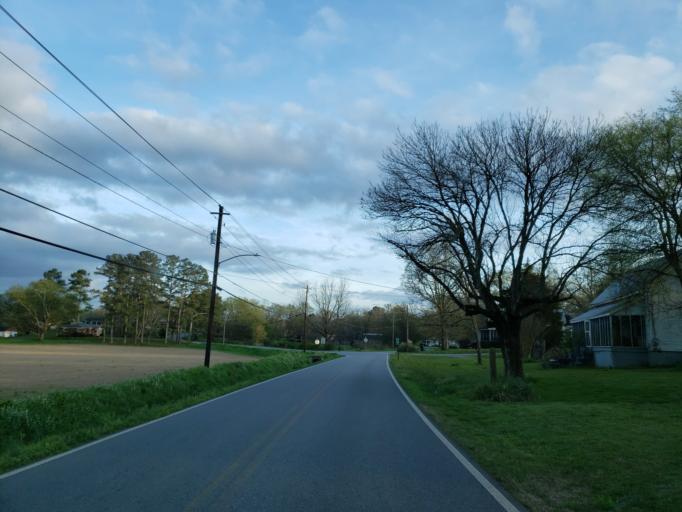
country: US
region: Georgia
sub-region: Polk County
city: Aragon
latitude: 34.0897
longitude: -84.9903
